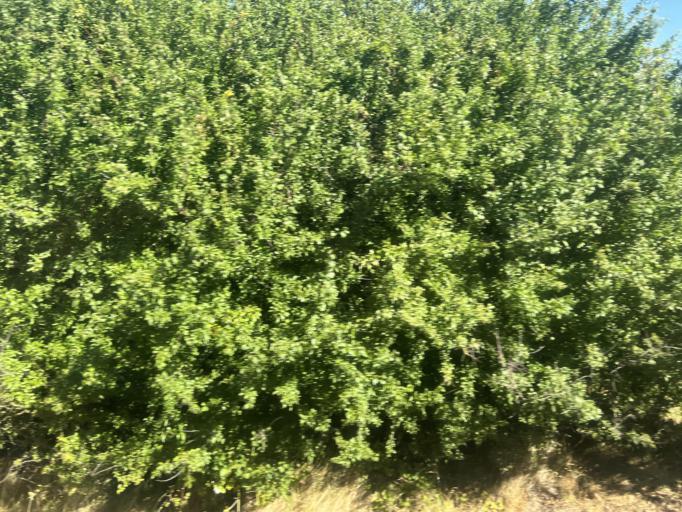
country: GB
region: England
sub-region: Lincolnshire
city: Sleaford
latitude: 52.9936
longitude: -0.3813
